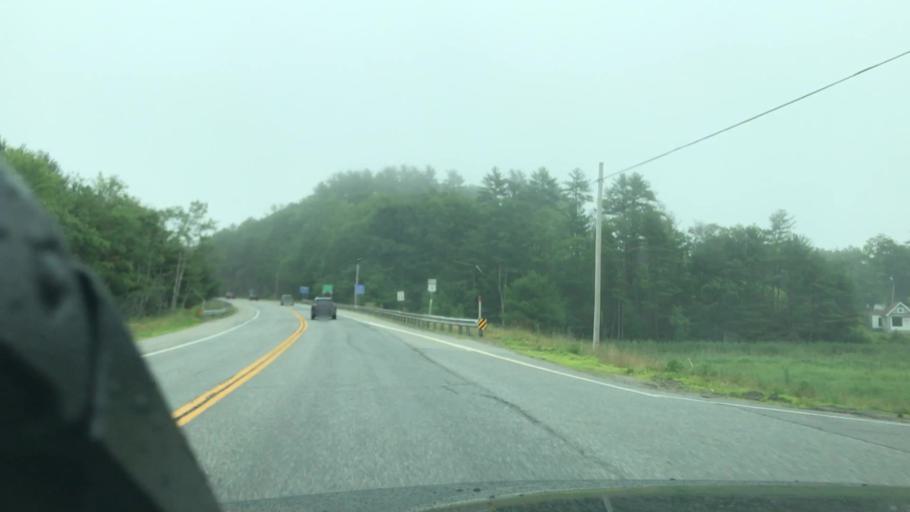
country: US
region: Maine
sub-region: Lincoln County
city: Damariscotta
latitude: 44.0277
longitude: -69.5517
